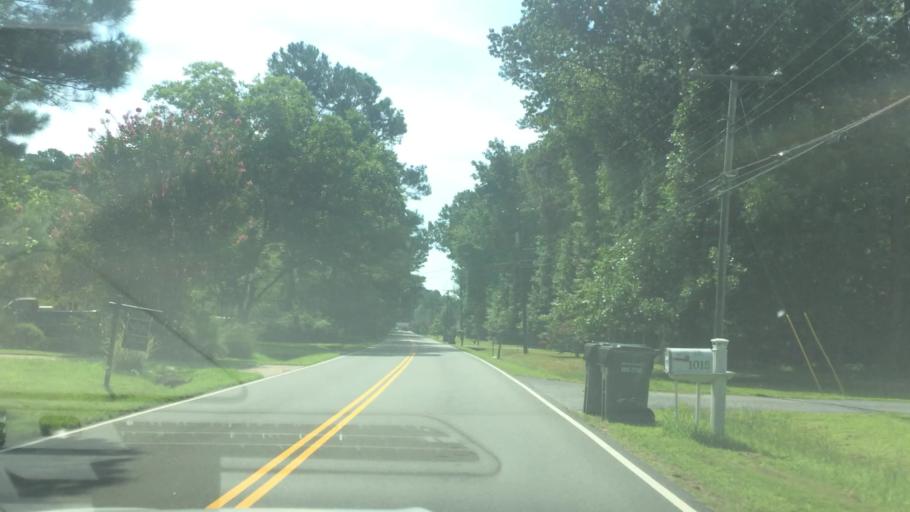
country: US
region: Virginia
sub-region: City of Poquoson
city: Poquoson
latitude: 37.1653
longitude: -76.4297
